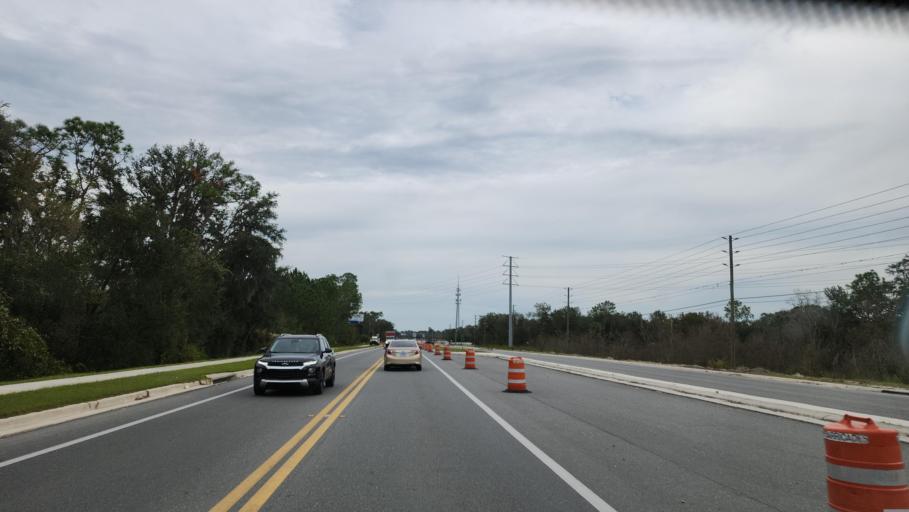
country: US
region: Florida
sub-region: Pasco County
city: Wesley Chapel
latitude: 28.2205
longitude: -82.2711
